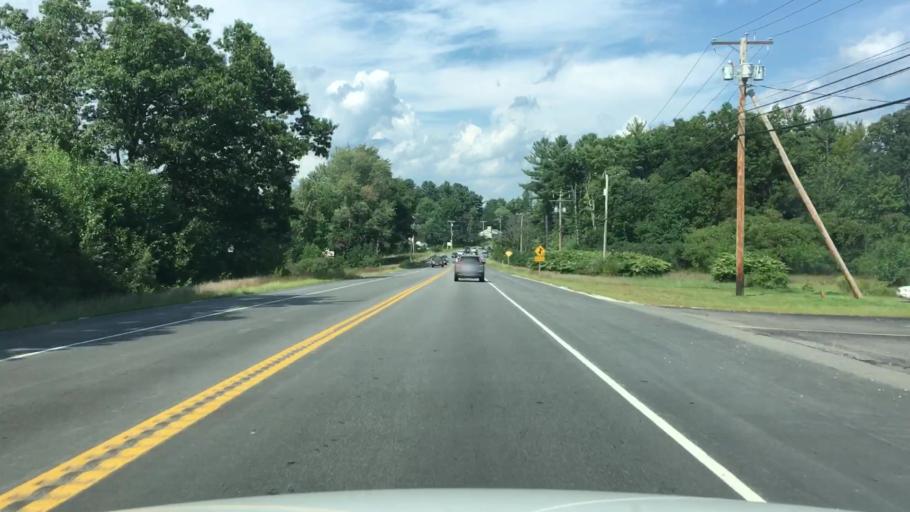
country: US
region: New Hampshire
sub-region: Rockingham County
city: Londonderry
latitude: 42.8546
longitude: -71.3565
